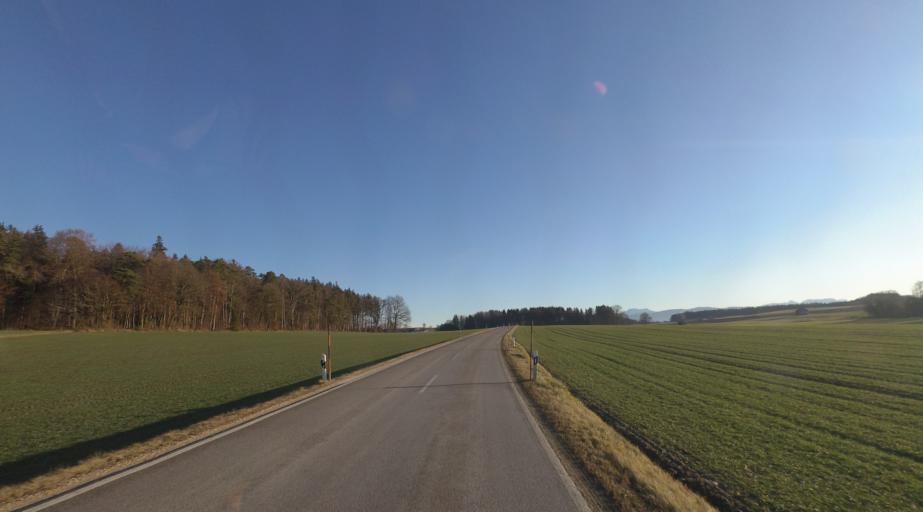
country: DE
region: Bavaria
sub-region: Upper Bavaria
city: Taching am See
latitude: 47.9901
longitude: 12.7666
